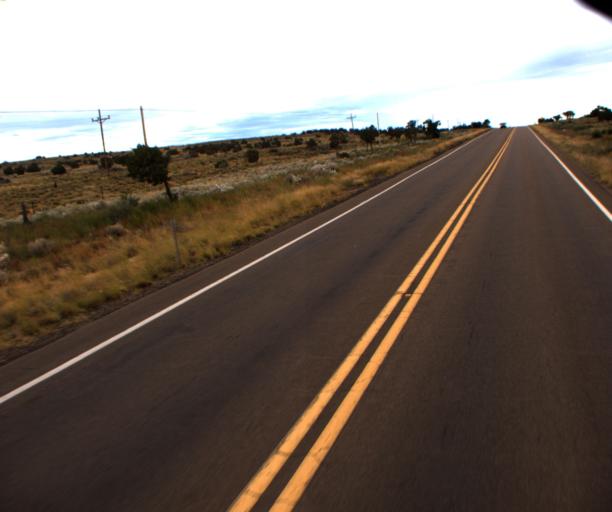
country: US
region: Arizona
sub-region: Navajo County
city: Snowflake
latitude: 34.5475
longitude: -110.0799
